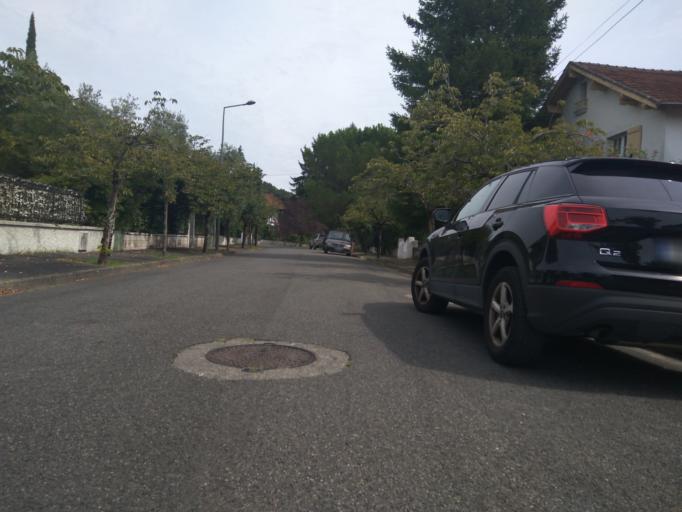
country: FR
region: Aquitaine
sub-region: Departement des Pyrenees-Atlantiques
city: Bizanos
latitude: 43.2935
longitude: -0.3519
